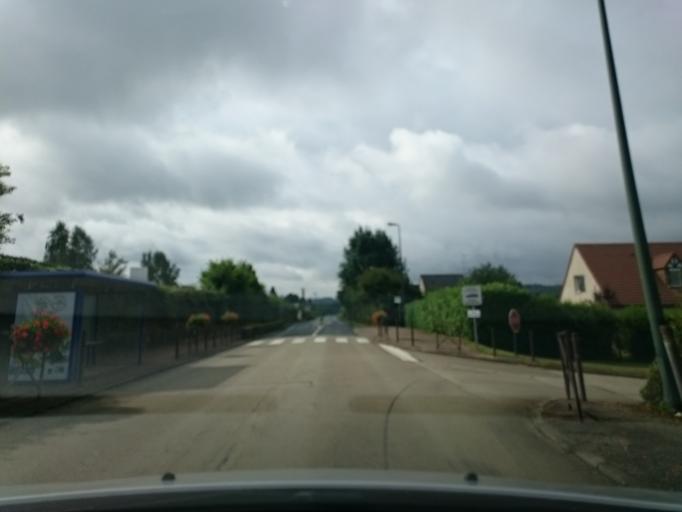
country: FR
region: Lower Normandy
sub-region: Departement du Calvados
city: Beuvillers
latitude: 49.1193
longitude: 0.2827
